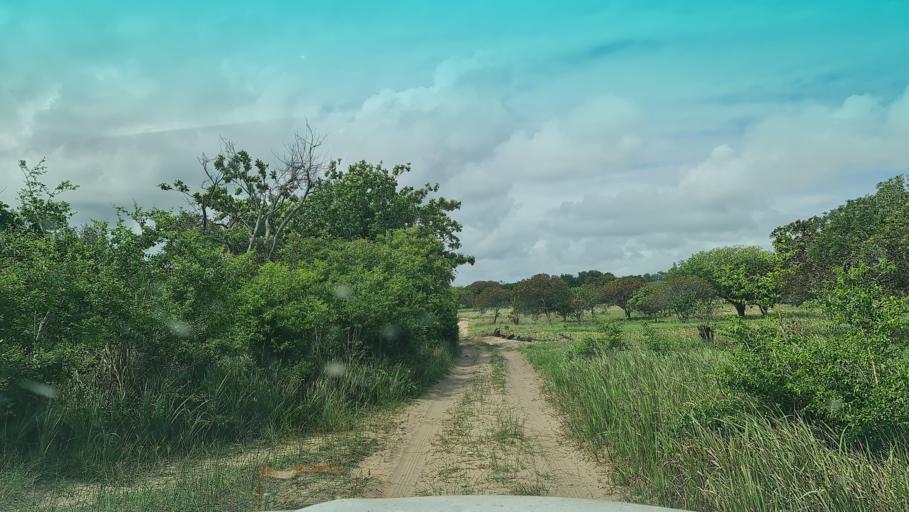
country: MZ
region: Maputo
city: Manhica
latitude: -25.3962
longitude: 33.0284
